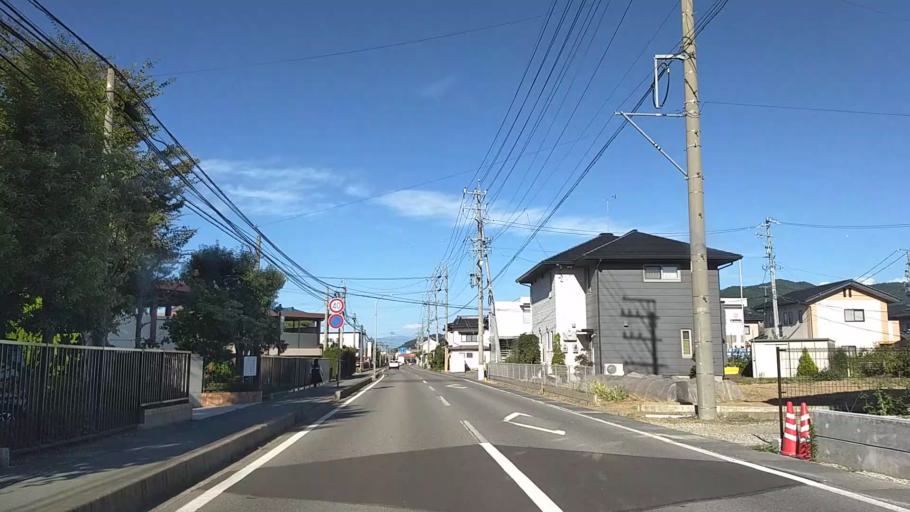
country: JP
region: Nagano
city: Nagano-shi
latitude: 36.5441
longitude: 138.1340
